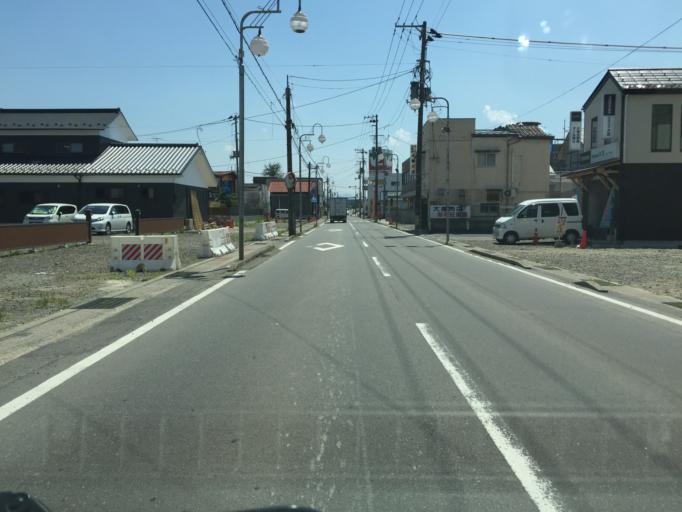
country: JP
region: Fukushima
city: Yanagawamachi-saiwaicho
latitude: 37.8585
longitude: 140.6080
